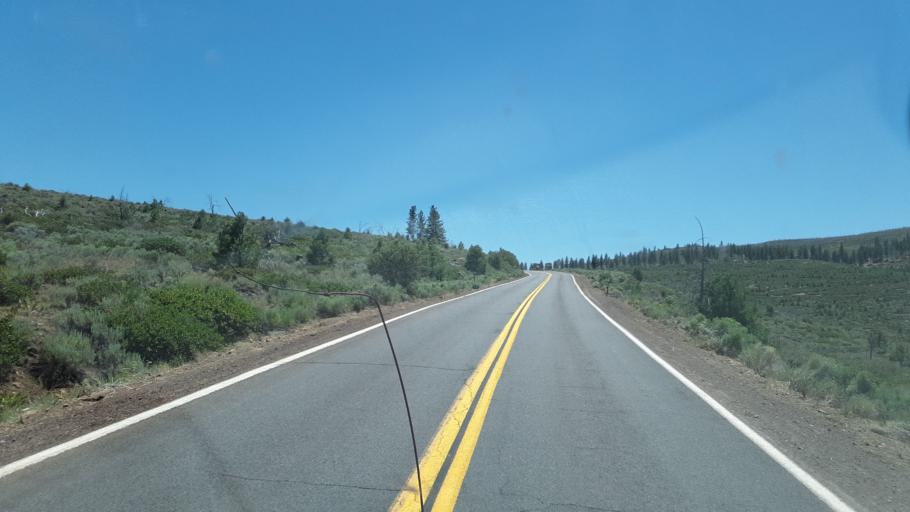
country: US
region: California
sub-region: Lassen County
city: Susanville
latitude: 40.6200
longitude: -120.6430
